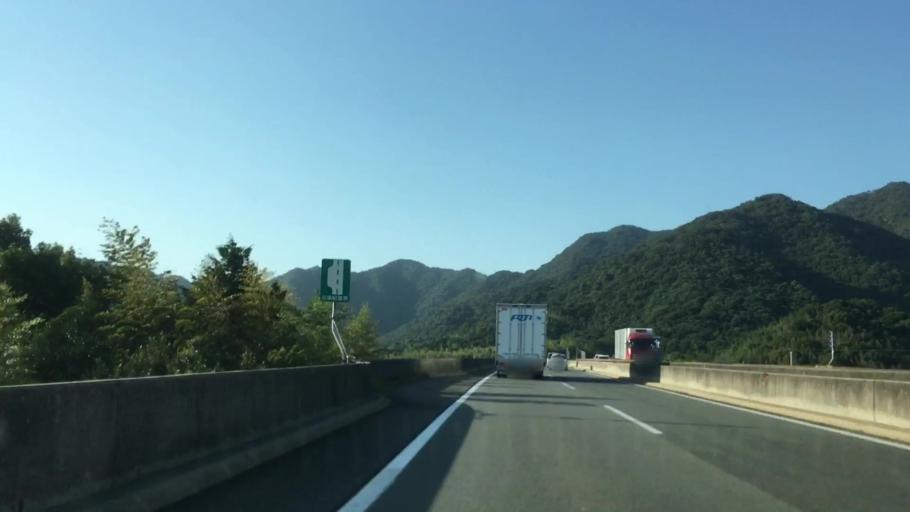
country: JP
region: Yamaguchi
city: Ogori-shimogo
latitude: 34.0954
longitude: 131.4540
